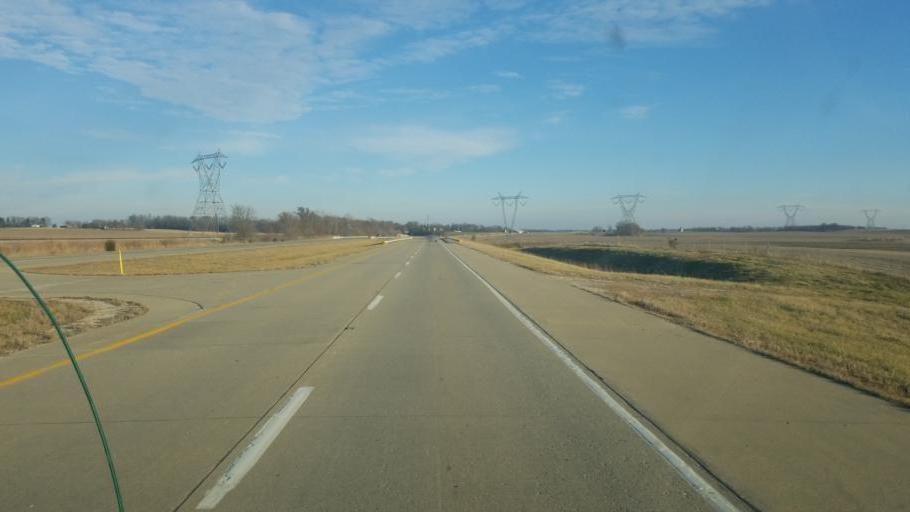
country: US
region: Indiana
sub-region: Knox County
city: Bicknell
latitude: 38.6688
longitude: -87.3380
